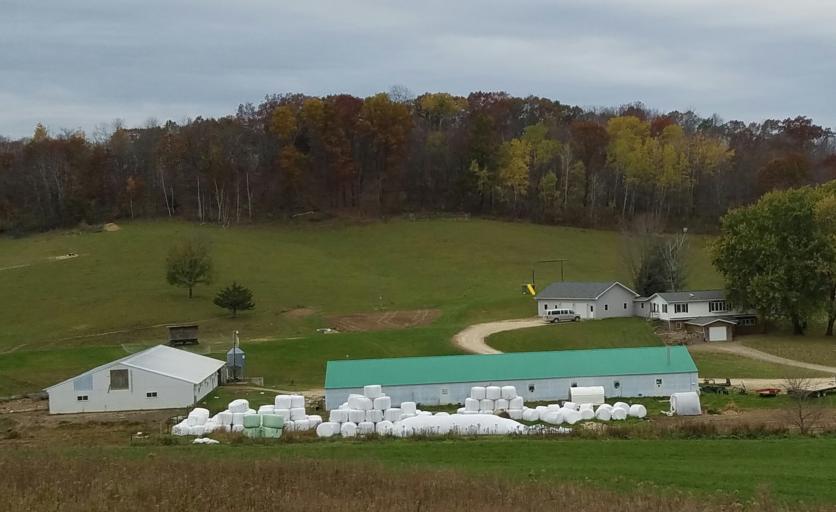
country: US
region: Wisconsin
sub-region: Vernon County
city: Hillsboro
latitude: 43.6255
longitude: -90.3363
